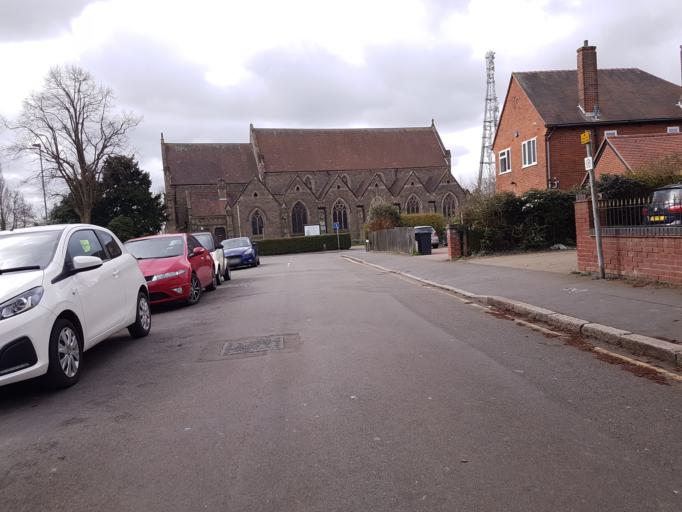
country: GB
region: England
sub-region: Leicestershire
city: Hinckley
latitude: 52.5418
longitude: -1.3770
